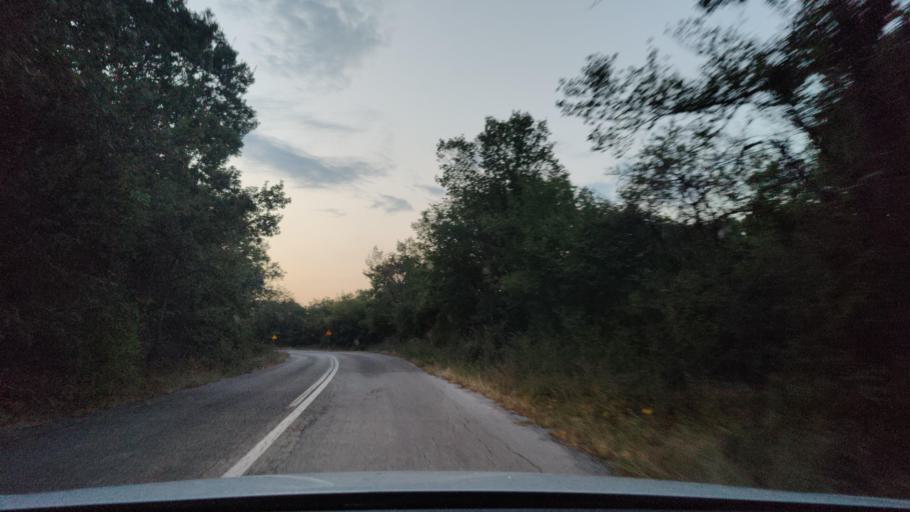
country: GR
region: Central Macedonia
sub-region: Nomos Serron
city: Chrysochorafa
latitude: 41.1796
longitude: 23.1619
